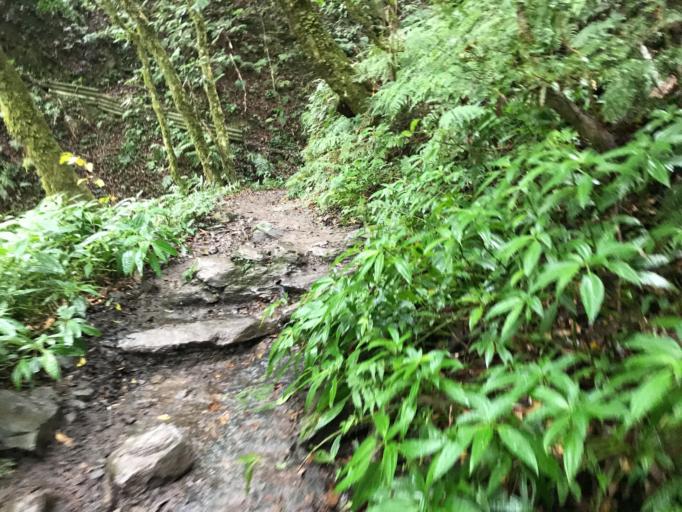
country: TW
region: Taiwan
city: Daxi
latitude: 24.5511
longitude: 121.2913
